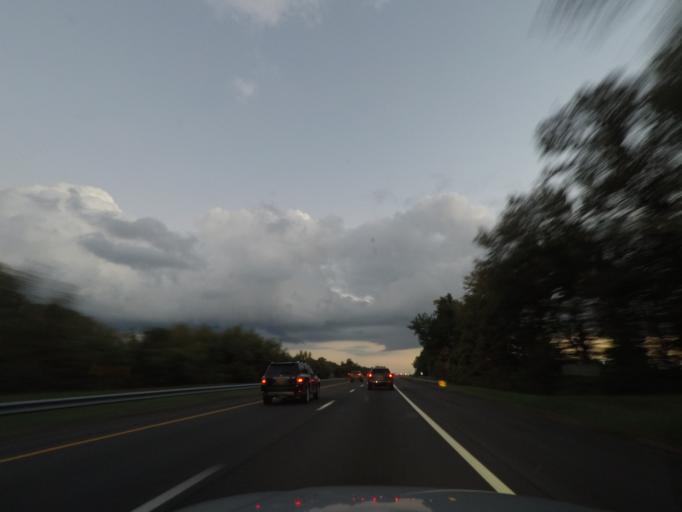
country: US
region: New York
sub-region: Ulster County
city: Plattekill
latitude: 41.6484
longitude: -74.0771
